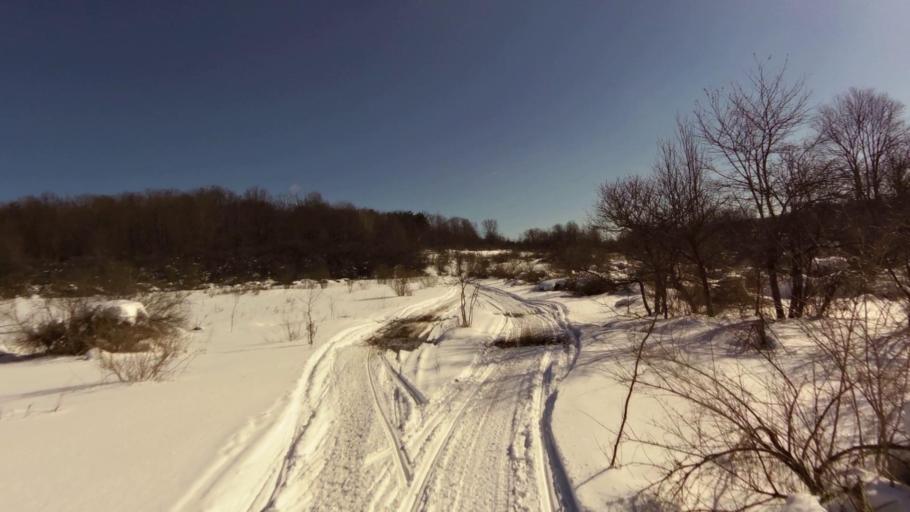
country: US
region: New York
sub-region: Cattaraugus County
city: Franklinville
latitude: 42.3467
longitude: -78.4372
